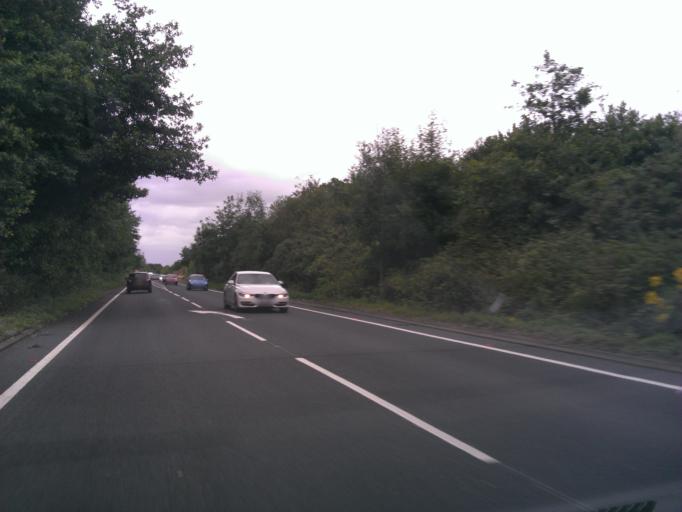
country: GB
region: England
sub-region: Essex
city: Little Clacton
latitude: 51.8436
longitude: 1.1101
